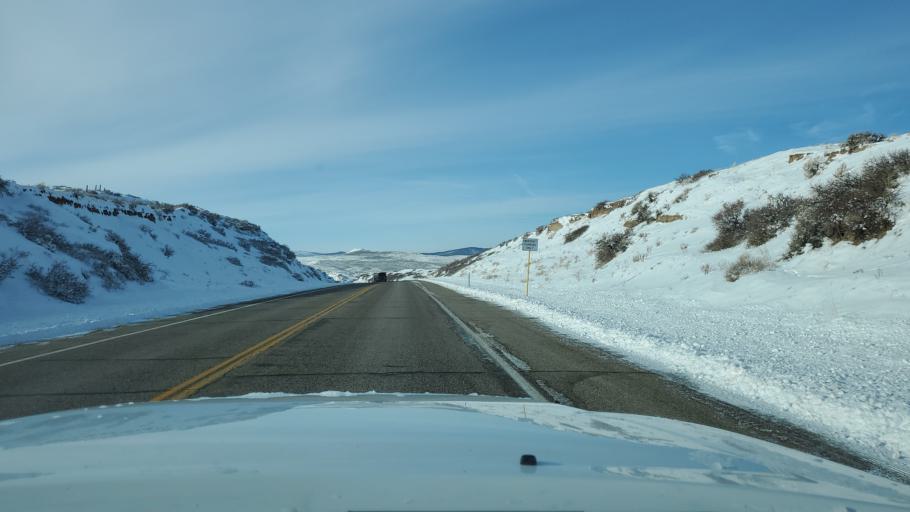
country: US
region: Colorado
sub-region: Rio Blanco County
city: Meeker
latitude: 40.4613
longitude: -108.2467
